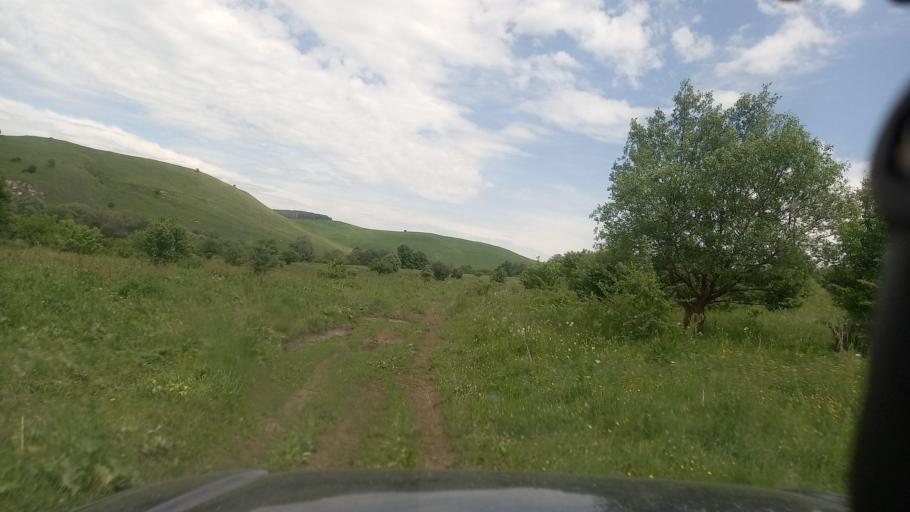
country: RU
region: Karachayevo-Cherkesiya
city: Pregradnaya
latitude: 44.0769
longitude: 41.2700
